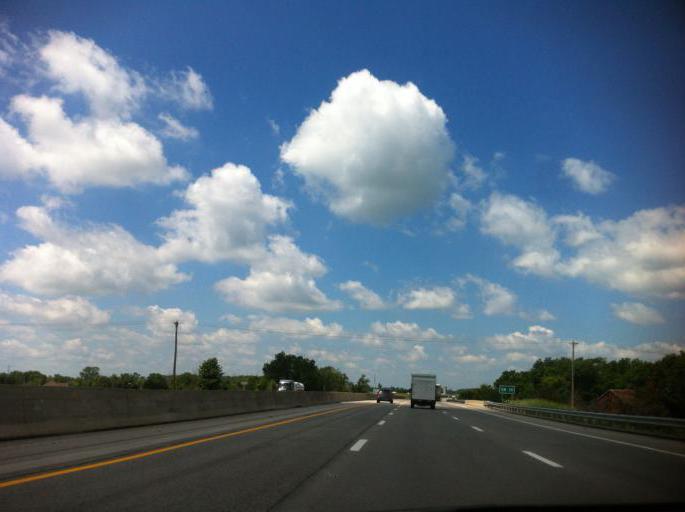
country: US
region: Ohio
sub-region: Sandusky County
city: Fremont
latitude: 41.4078
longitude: -83.1347
